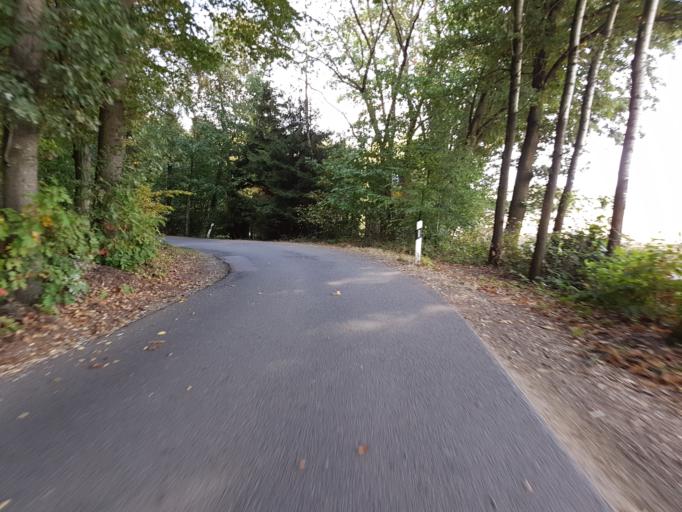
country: DE
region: Saxony
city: Claussnitz
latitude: 50.9507
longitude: 12.8793
